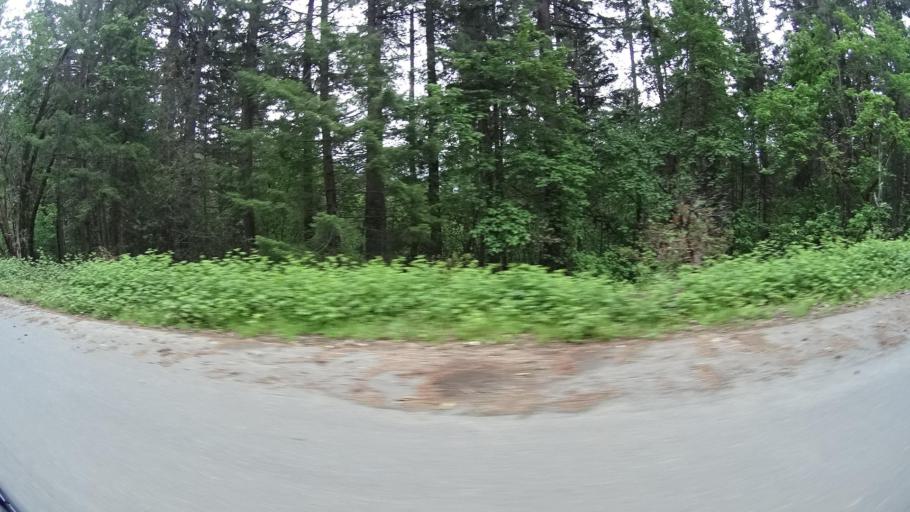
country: US
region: California
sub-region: Humboldt County
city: Willow Creek
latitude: 41.1186
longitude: -123.7315
